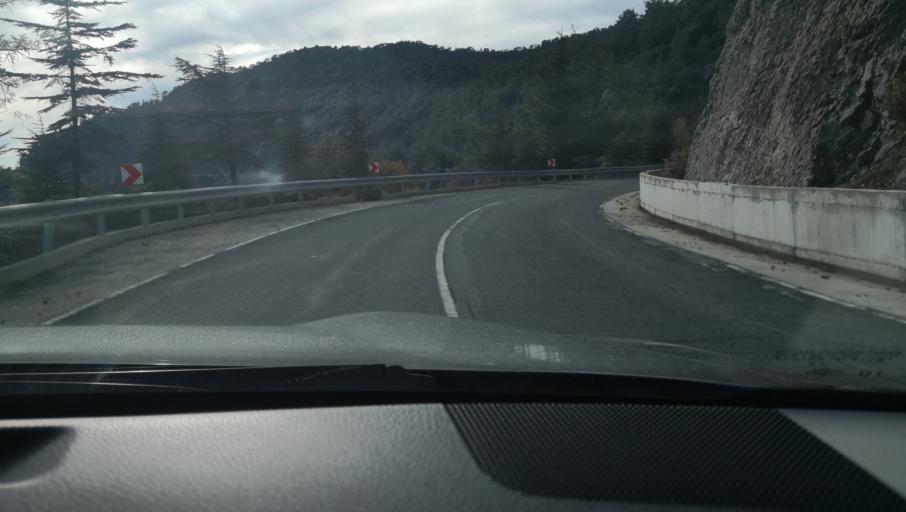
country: CY
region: Lefkosia
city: Lefka
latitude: 34.9929
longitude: 32.7379
